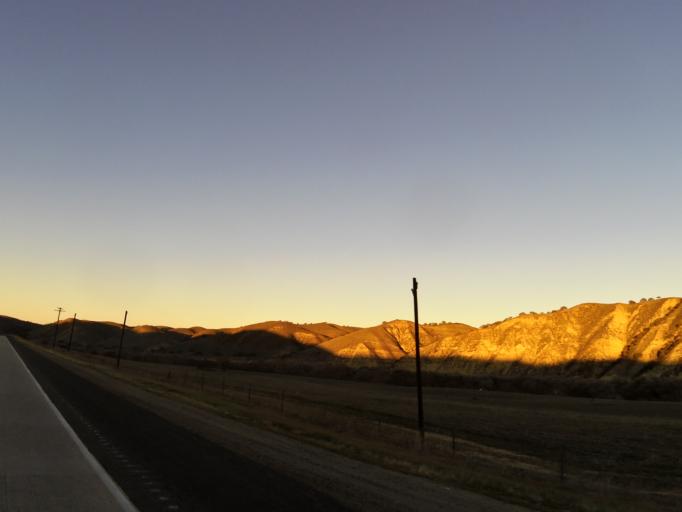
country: US
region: California
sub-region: San Luis Obispo County
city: Lake Nacimiento
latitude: 35.8943
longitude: -120.8416
